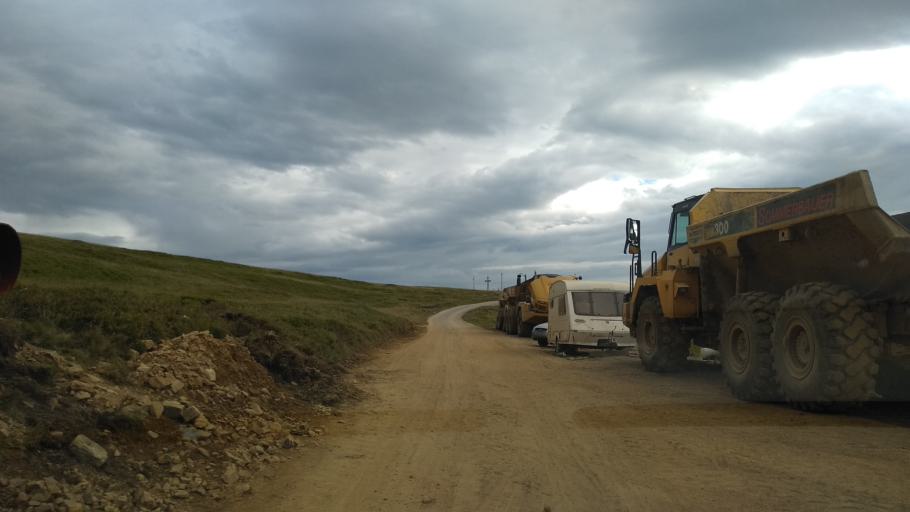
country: RO
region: Hunedoara
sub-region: Municipiul  Vulcan
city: Jiu-Paroseni
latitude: 45.3017
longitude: 23.3118
